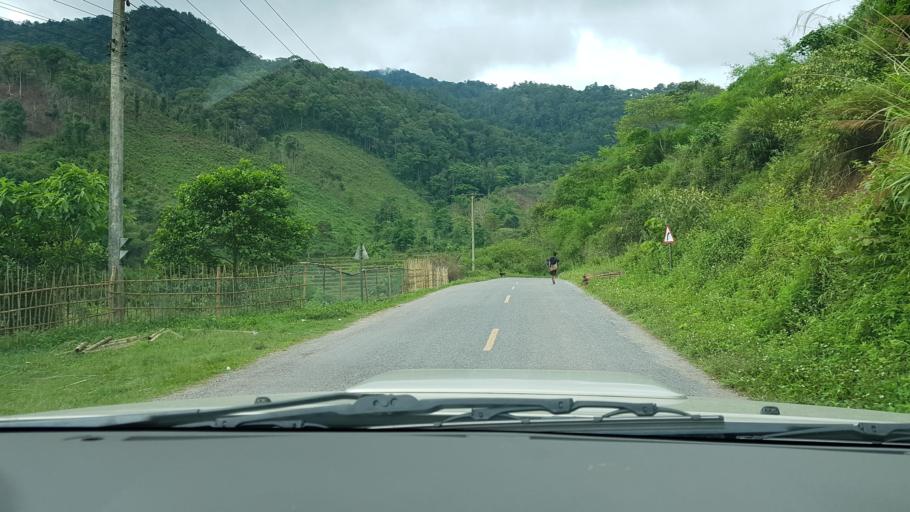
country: LA
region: Oudomxai
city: Muang Xay
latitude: 20.5563
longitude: 101.9117
